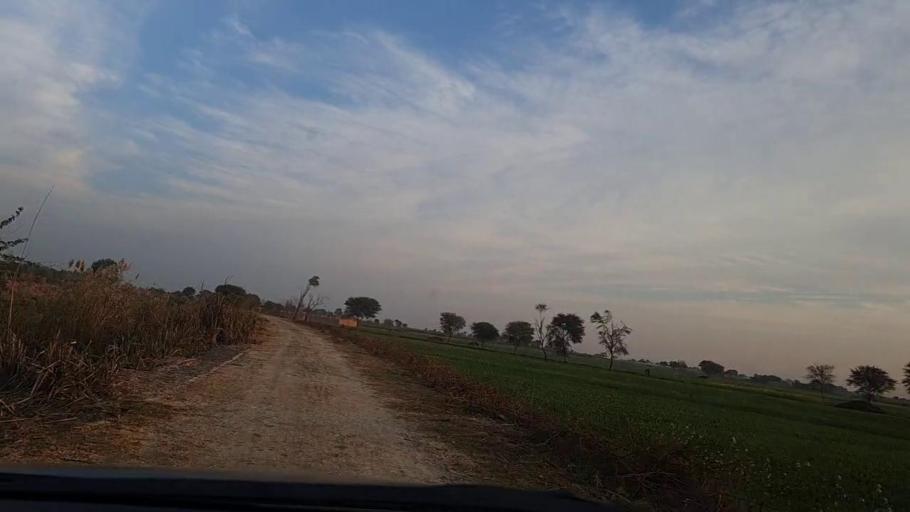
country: PK
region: Sindh
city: Sakrand
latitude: 26.1719
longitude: 68.3472
